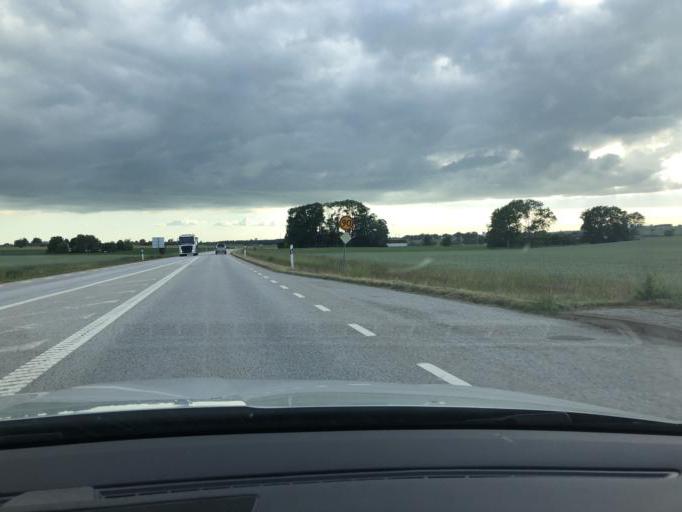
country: SE
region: Skane
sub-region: Simrishamns Kommun
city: Simrishamn
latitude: 55.5378
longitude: 14.3177
